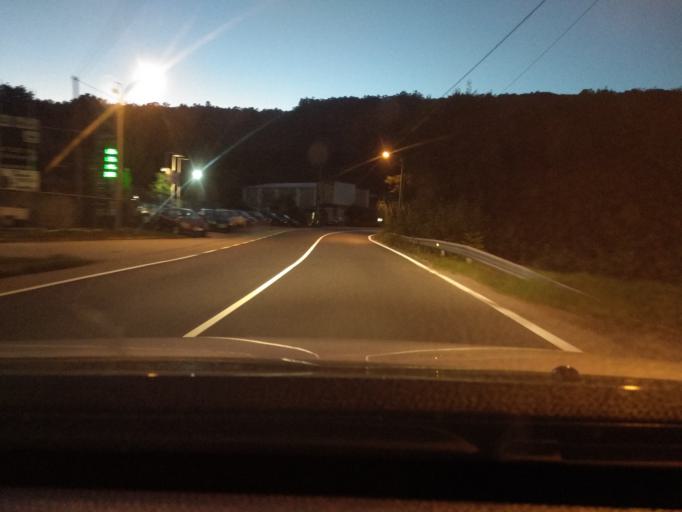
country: ES
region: Galicia
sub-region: Provincia de Pontevedra
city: Moana
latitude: 42.2892
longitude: -8.7428
